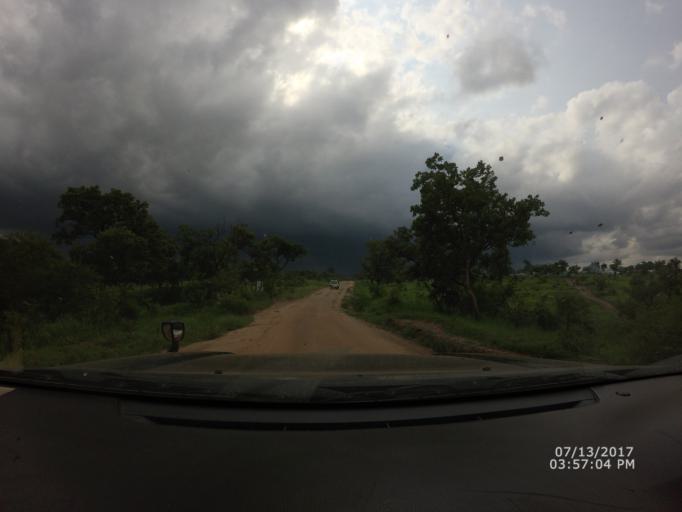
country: UG
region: Northern Region
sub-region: Yumbe District
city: Yumbe
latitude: 3.2932
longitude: 31.3035
